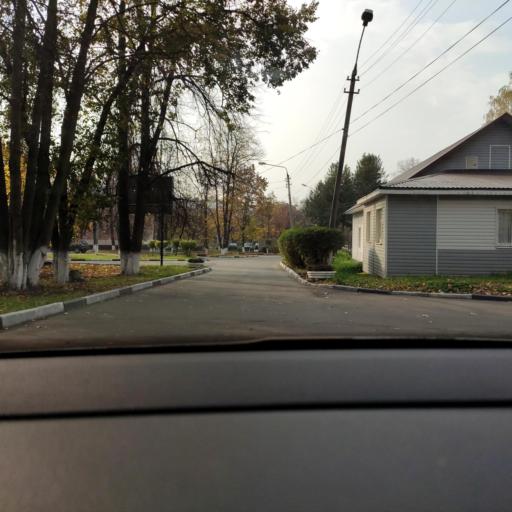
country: RU
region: Moskovskaya
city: Ivanteyevka
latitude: 55.9782
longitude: 37.9047
